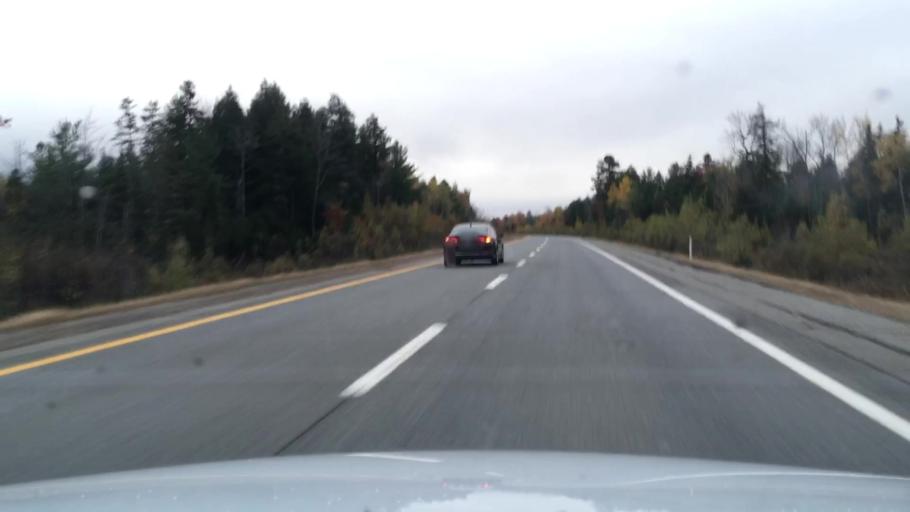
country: US
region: Maine
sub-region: Penobscot County
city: Greenbush
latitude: 45.1025
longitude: -68.6961
